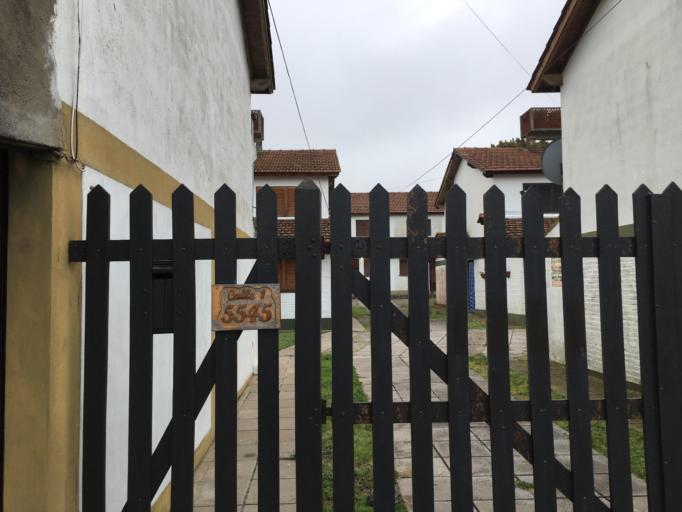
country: AR
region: Buenos Aires
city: Mar del Tuyu
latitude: -36.5563
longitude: -56.6897
